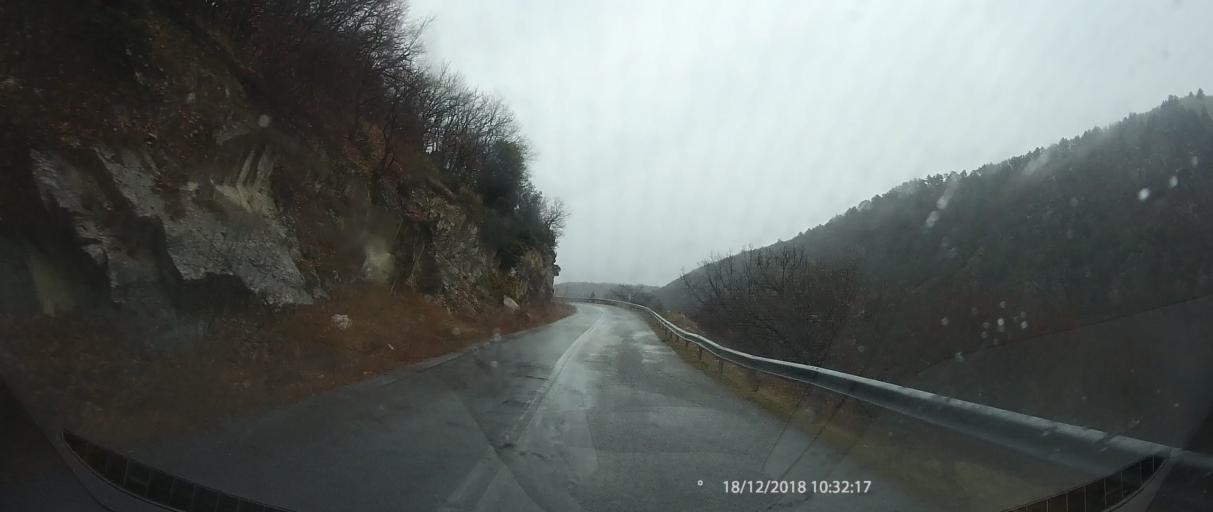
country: GR
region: Central Macedonia
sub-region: Nomos Pierias
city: Kato Milia
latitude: 40.1908
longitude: 22.2906
